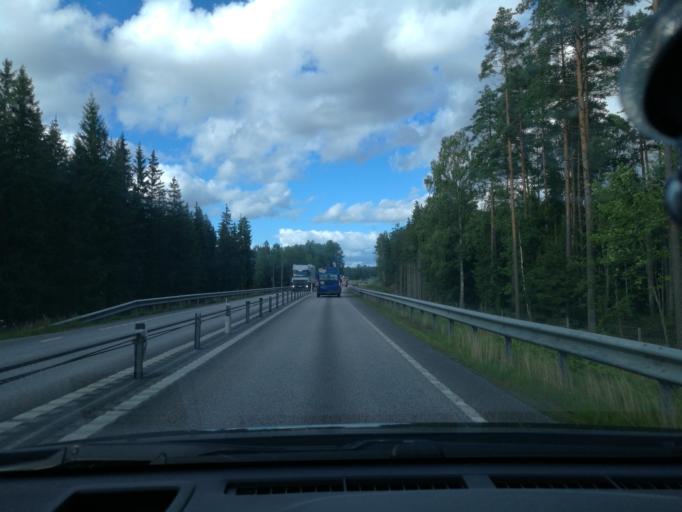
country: SE
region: Kronoberg
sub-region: Vaxjo Kommun
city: Braas
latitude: 57.0293
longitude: 15.0634
